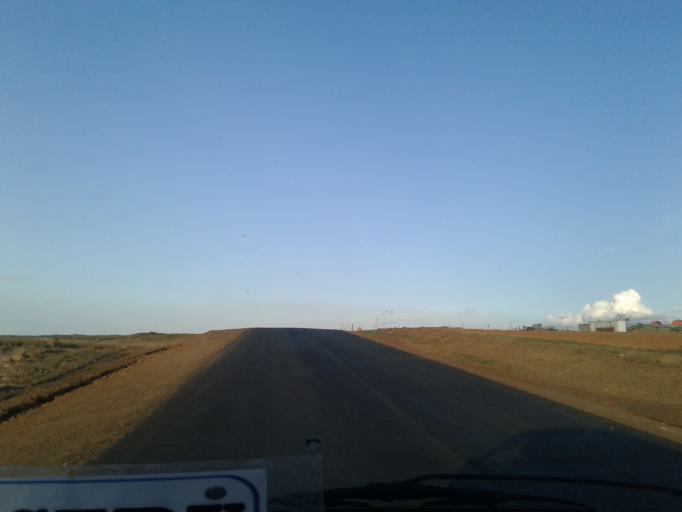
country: LS
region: Maseru
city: Maseru
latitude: -29.3112
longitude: 27.5980
